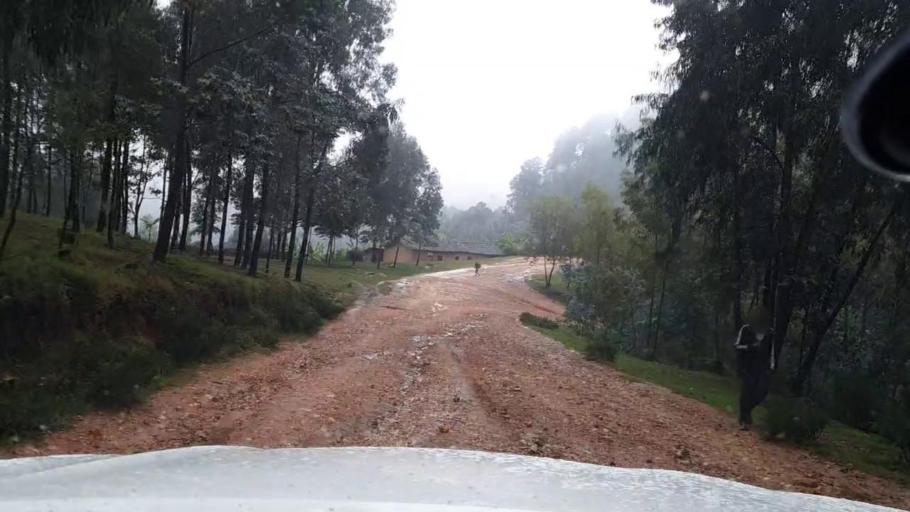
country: RW
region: Western Province
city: Kibuye
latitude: -2.1362
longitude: 29.4649
